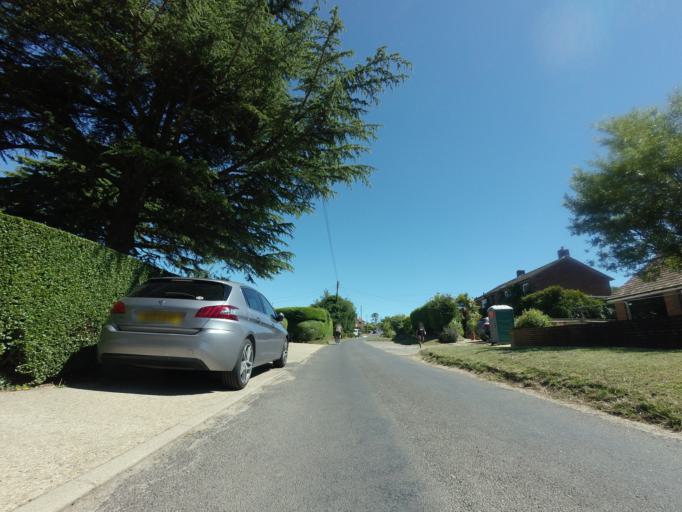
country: GB
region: England
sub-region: Kent
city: Eastry
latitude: 51.1992
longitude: 1.3215
